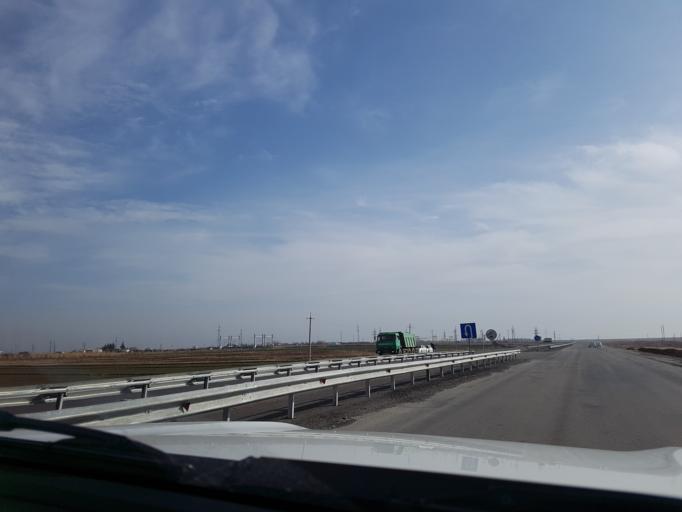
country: IR
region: Razavi Khorasan
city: Sarakhs
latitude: 37.2229
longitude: 61.2231
